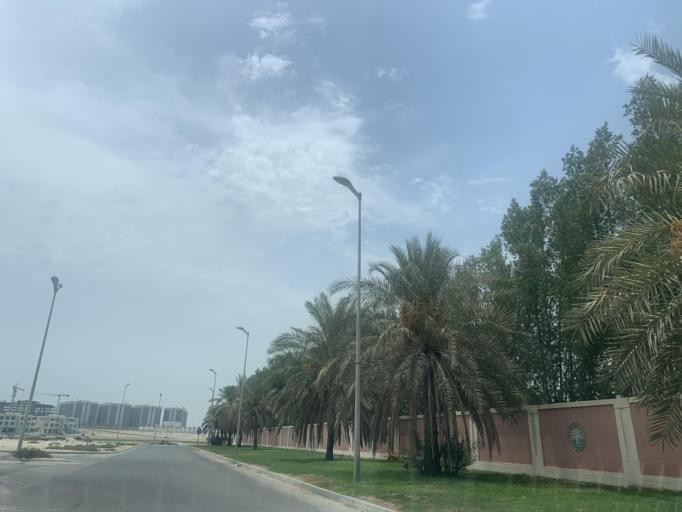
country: BH
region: Muharraq
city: Al Hadd
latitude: 26.2768
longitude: 50.6678
